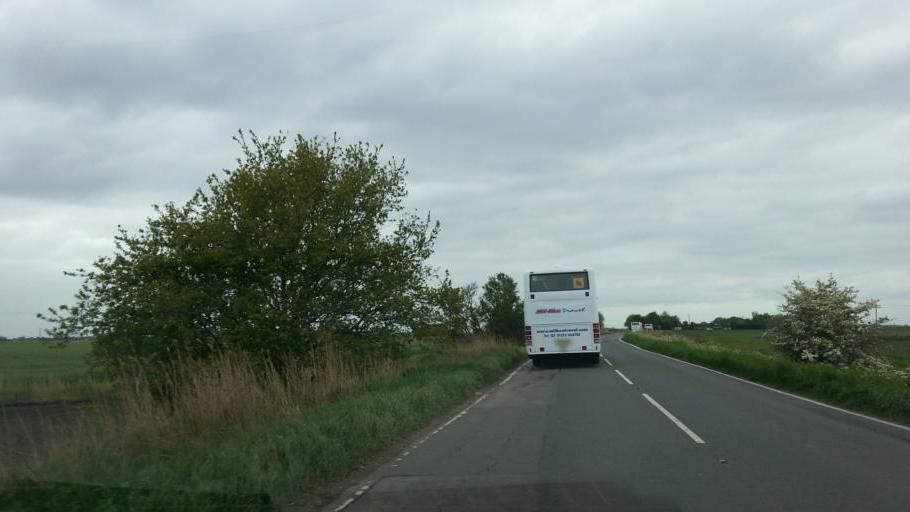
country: GB
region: England
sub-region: Cambridgeshire
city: Isleham
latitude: 52.4332
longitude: 0.4052
